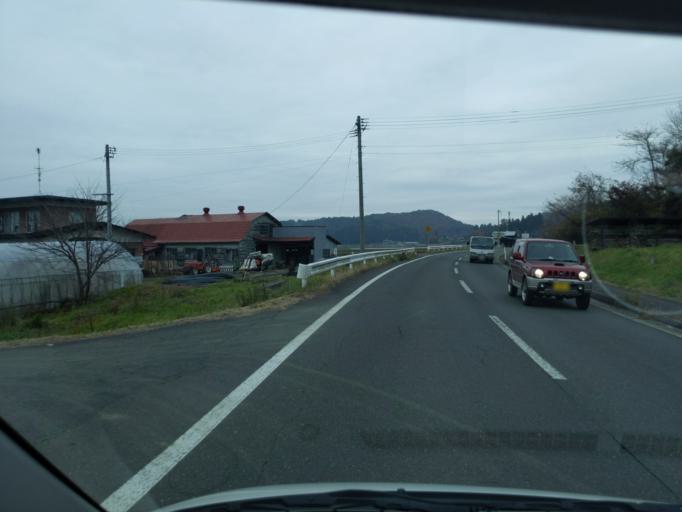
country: JP
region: Iwate
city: Mizusawa
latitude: 39.1713
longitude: 141.2130
